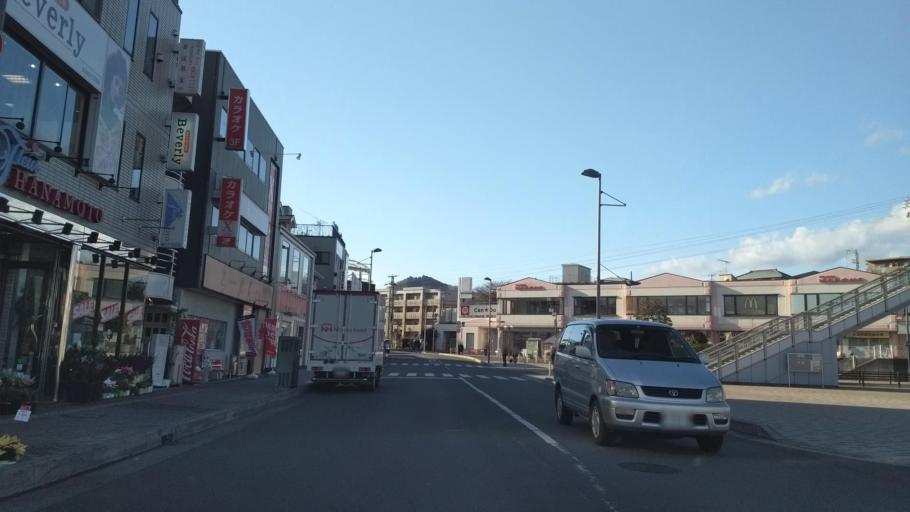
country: JP
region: Kanagawa
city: Isehara
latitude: 35.3724
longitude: 139.2718
